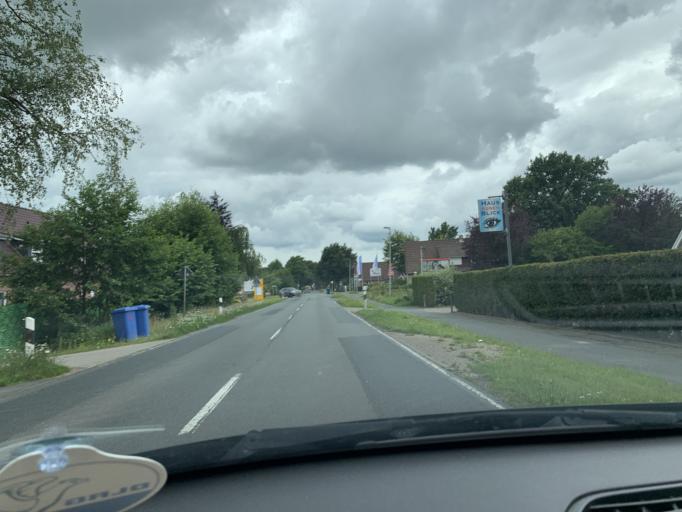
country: DE
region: Lower Saxony
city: Edewecht
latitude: 53.1175
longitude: 7.9650
